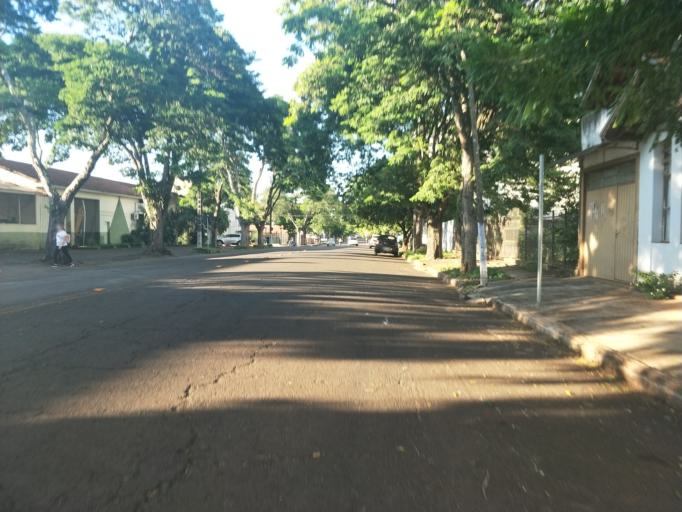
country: BR
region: Parana
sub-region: Marechal Candido Rondon
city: Marechal Candido Rondon
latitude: -24.5560
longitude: -54.0589
